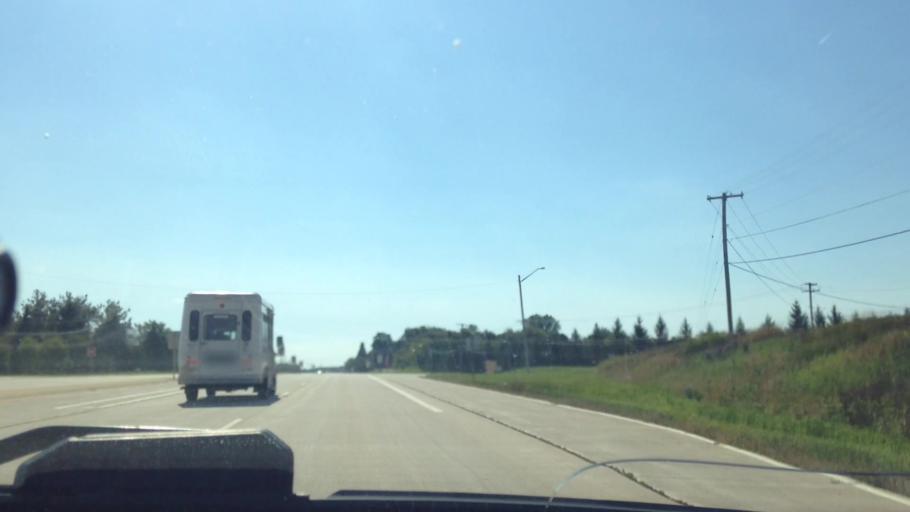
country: US
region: Wisconsin
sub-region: Ozaukee County
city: Saukville
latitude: 43.3537
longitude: -87.9134
